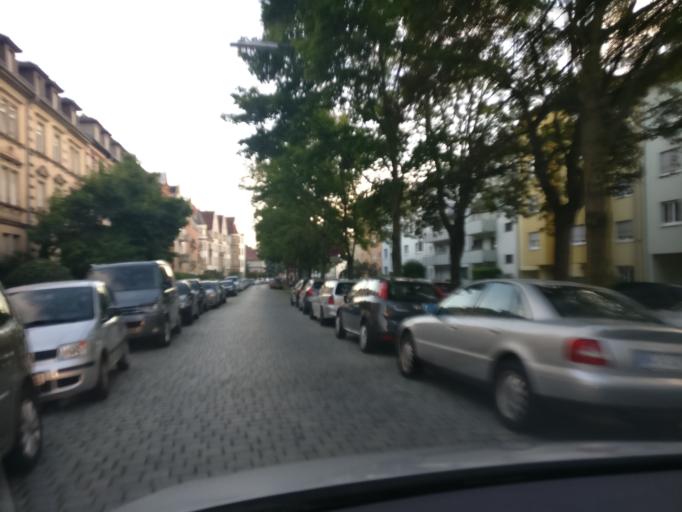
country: DE
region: Baden-Wuerttemberg
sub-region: Karlsruhe Region
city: Weingarten
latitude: 49.0020
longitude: 8.4785
